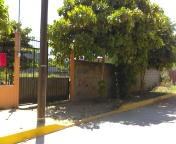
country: MX
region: Oaxaca
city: Asuncion Ixtaltepec
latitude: 16.5060
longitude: -95.0591
